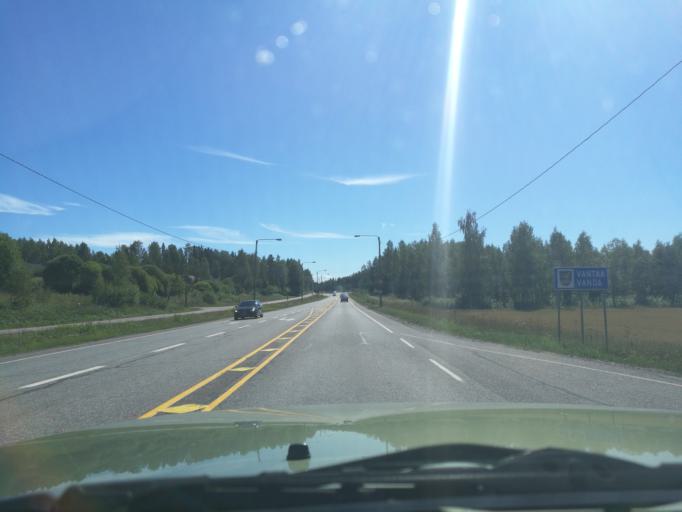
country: FI
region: Uusimaa
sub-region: Helsinki
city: Kerava
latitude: 60.3595
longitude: 25.1278
